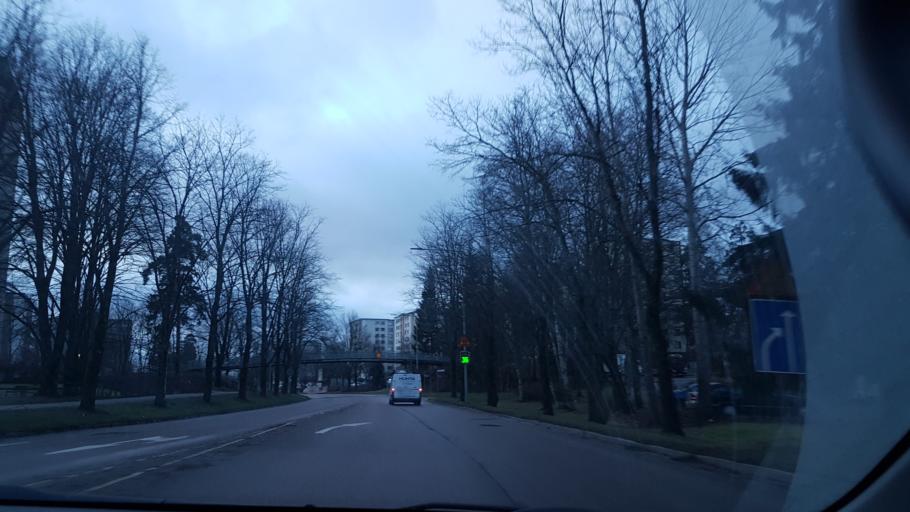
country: FI
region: Uusimaa
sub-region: Helsinki
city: Vantaa
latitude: 60.2774
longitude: 25.1051
